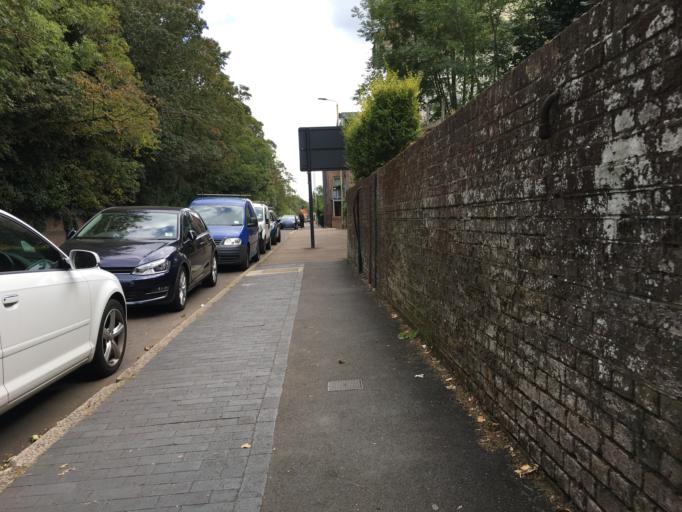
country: GB
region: England
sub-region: Hertfordshire
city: St Albans
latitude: 51.7471
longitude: -0.3306
